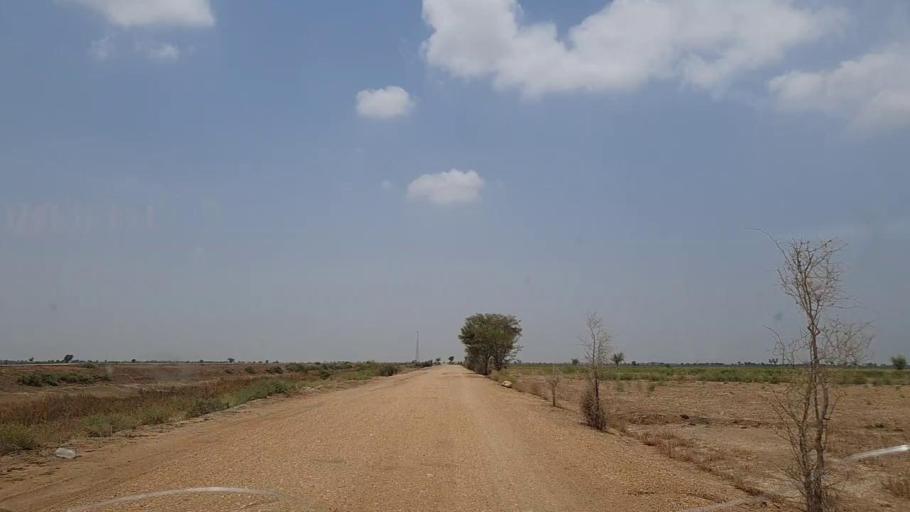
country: PK
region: Sindh
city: Johi
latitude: 26.7752
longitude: 67.6539
